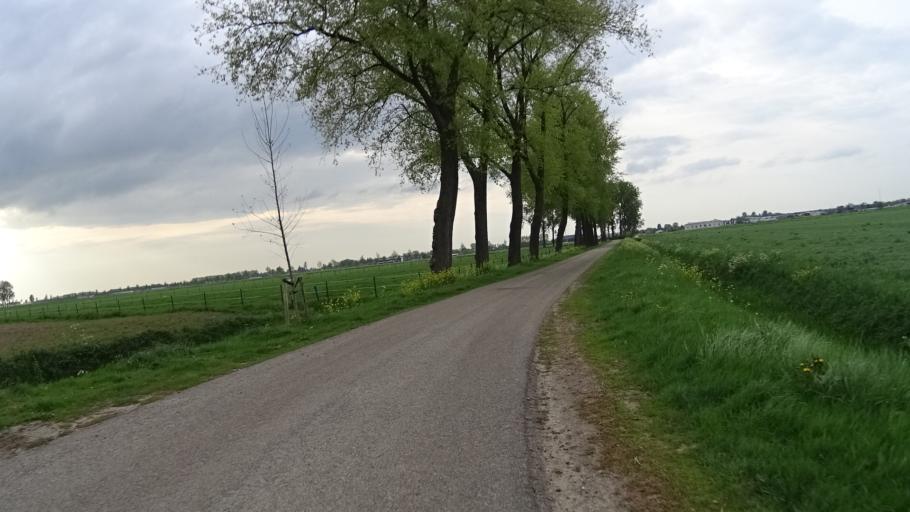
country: NL
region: North Brabant
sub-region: Gemeente Aalburg
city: Aalburg
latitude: 51.7638
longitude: 5.0986
